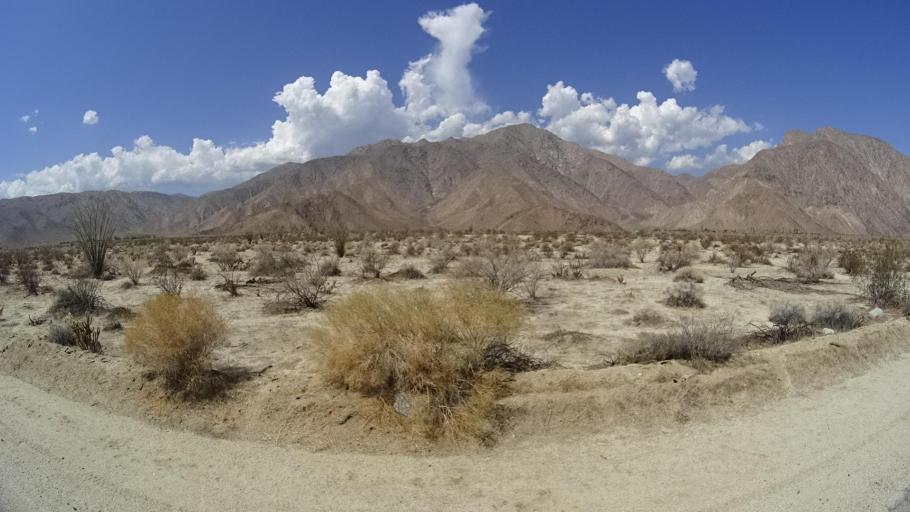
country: US
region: California
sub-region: San Diego County
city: Borrego Springs
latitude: 33.2632
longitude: -116.3996
